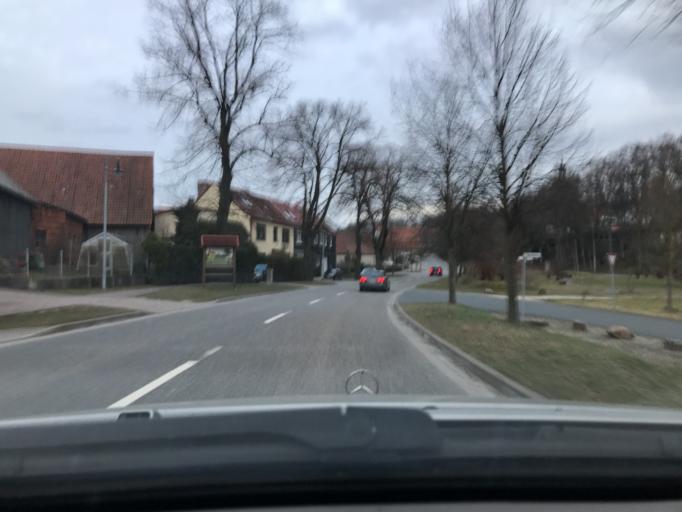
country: DE
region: Thuringia
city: Kreuzebra
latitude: 51.3435
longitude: 10.2524
